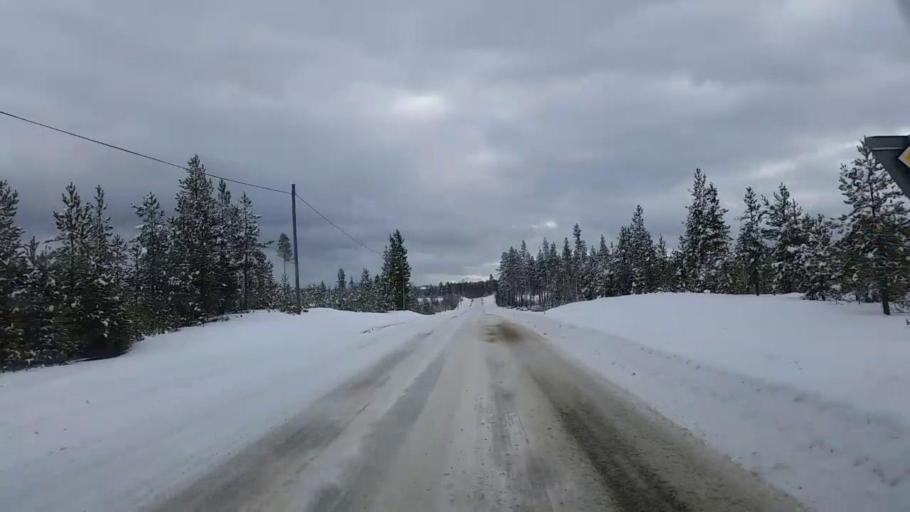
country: SE
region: Jaemtland
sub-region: Harjedalens Kommun
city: Sveg
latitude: 62.1279
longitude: 14.9779
